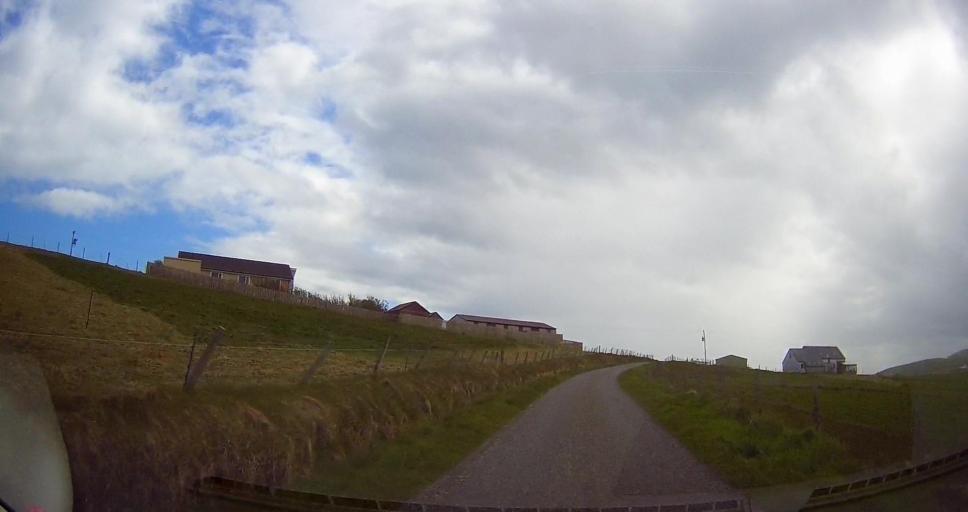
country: GB
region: Scotland
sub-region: Shetland Islands
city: Sandwick
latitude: 59.9175
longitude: -1.3203
